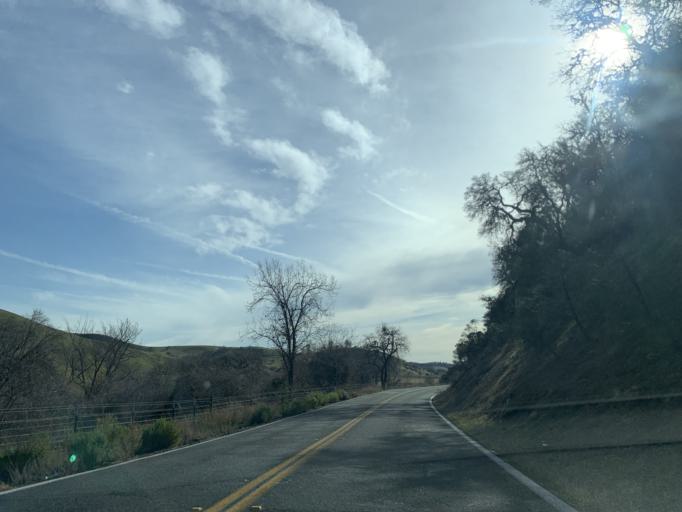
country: US
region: California
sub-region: Monterey County
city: Soledad
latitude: 36.5519
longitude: -121.1613
